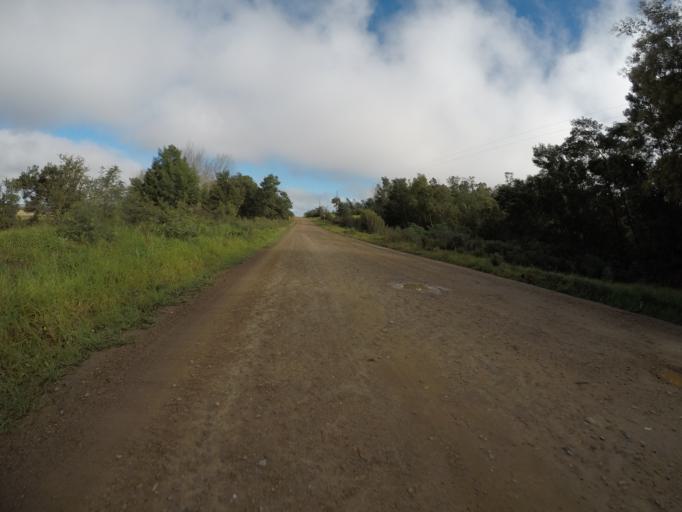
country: ZA
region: Western Cape
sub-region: Cape Winelands District Municipality
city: Ashton
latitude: -34.1114
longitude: 19.7965
